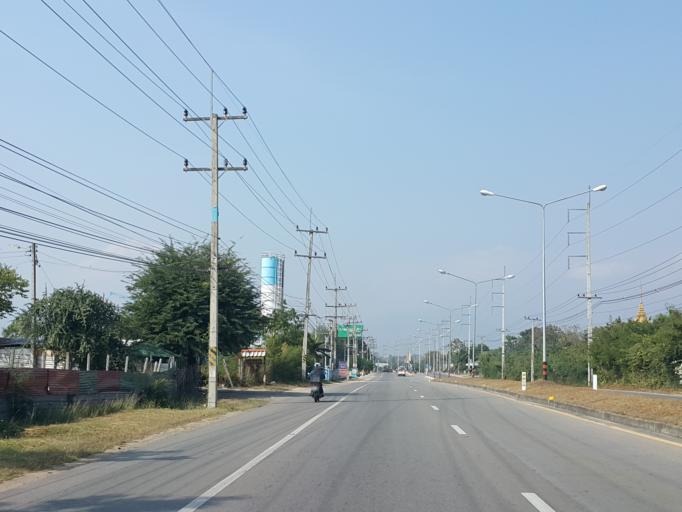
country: TH
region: Lamphun
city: Wiang Nong Long
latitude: 18.4517
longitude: 98.7225
